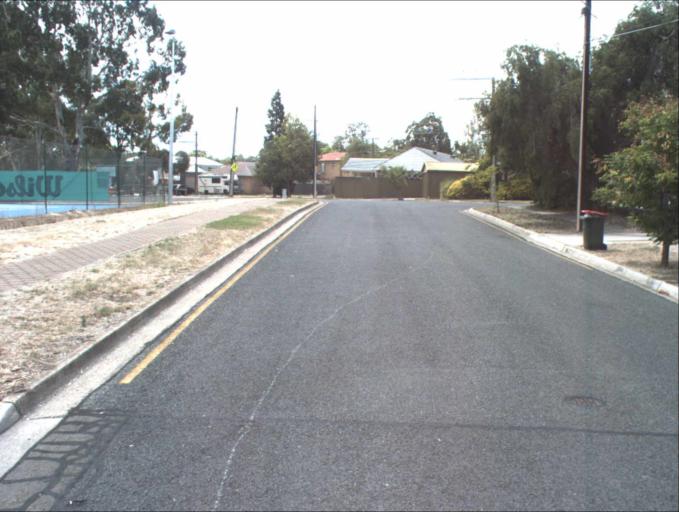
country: AU
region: South Australia
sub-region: Tea Tree Gully
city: Modbury
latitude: -34.8400
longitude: 138.6665
